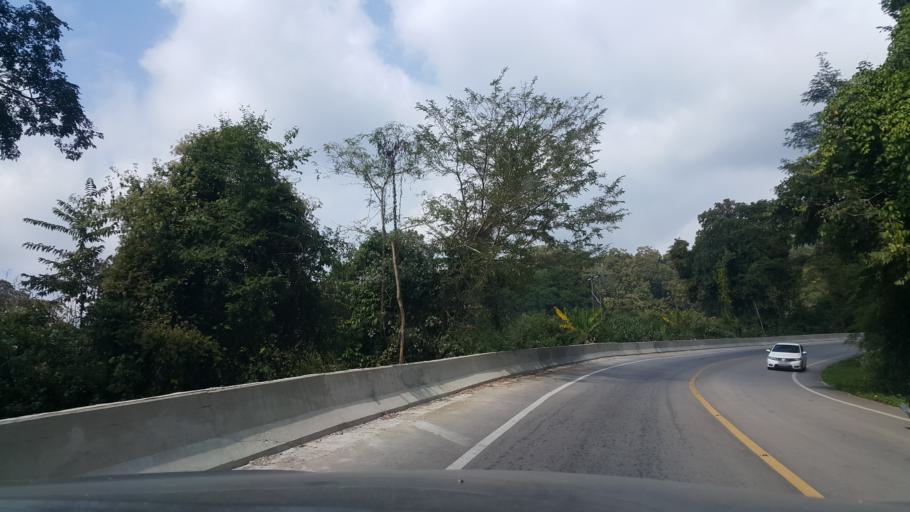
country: TH
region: Lampang
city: Wang Nuea
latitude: 19.0650
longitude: 99.7313
